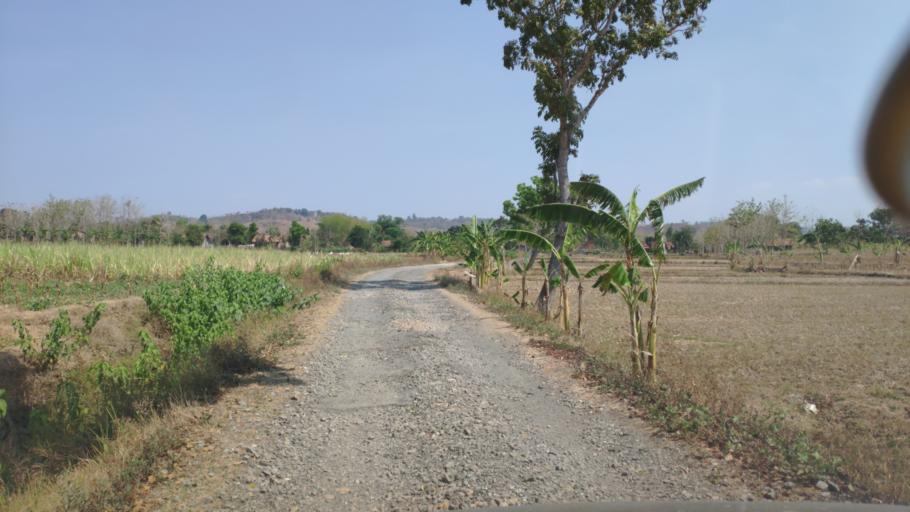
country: ID
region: Central Java
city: Ngundaan
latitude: -6.9165
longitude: 111.3949
